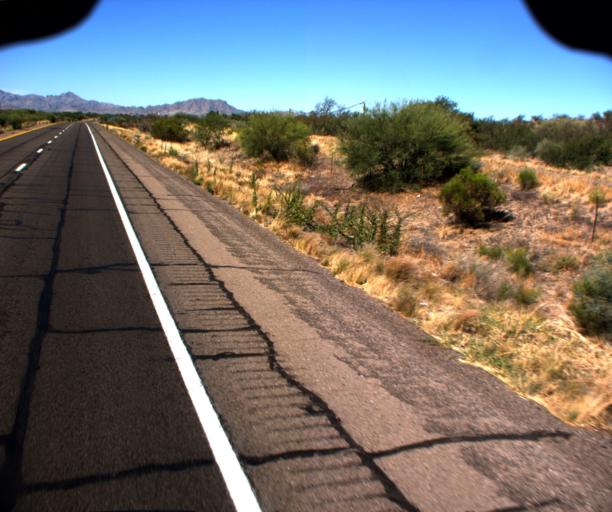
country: US
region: Arizona
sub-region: Pima County
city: Arivaca Junction
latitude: 31.7489
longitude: -111.0448
